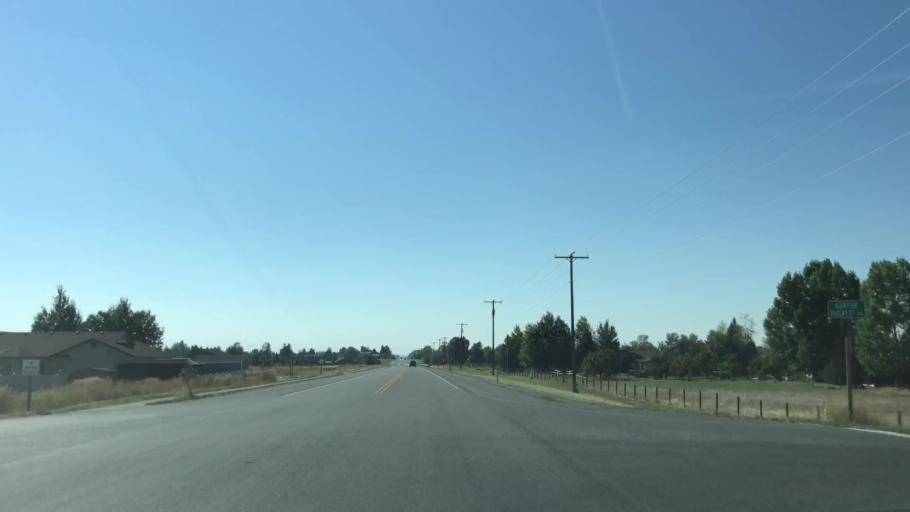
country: US
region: Montana
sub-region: Gallatin County
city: Belgrade
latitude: 45.7294
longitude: -111.1239
